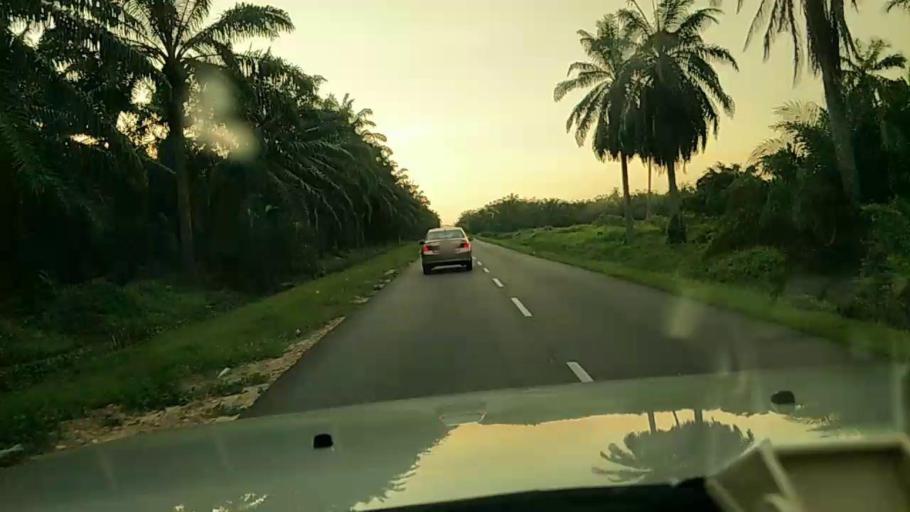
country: MY
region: Selangor
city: Kuala Selangor
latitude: 3.3175
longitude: 101.2798
